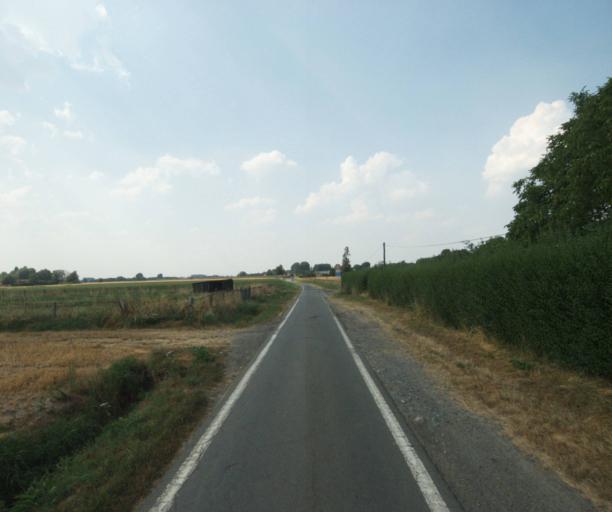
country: FR
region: Nord-Pas-de-Calais
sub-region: Departement du Nord
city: Linselles
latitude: 50.7208
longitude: 3.0594
